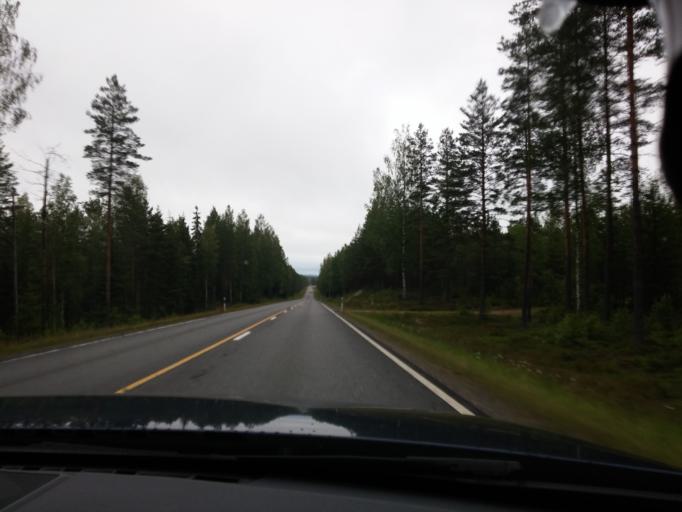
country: FI
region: Pirkanmaa
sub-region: Ylae-Pirkanmaa
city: Vilppula
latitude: 61.9356
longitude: 24.5405
